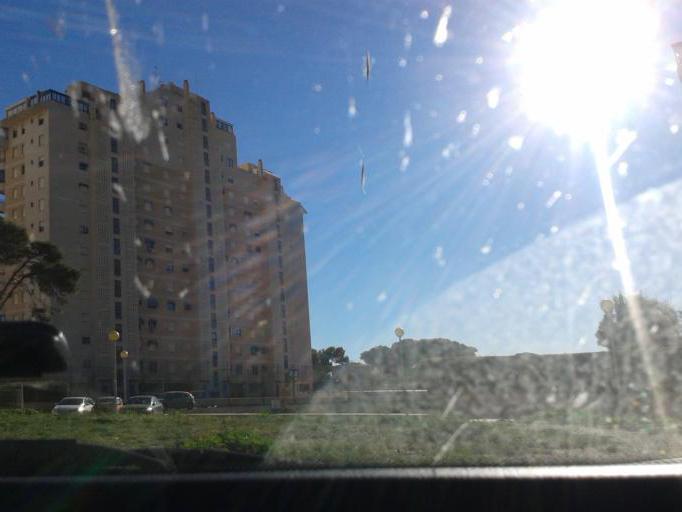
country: ES
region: Valencia
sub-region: Provincia de Alicante
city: el Campello
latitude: 38.4030
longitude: -0.4073
